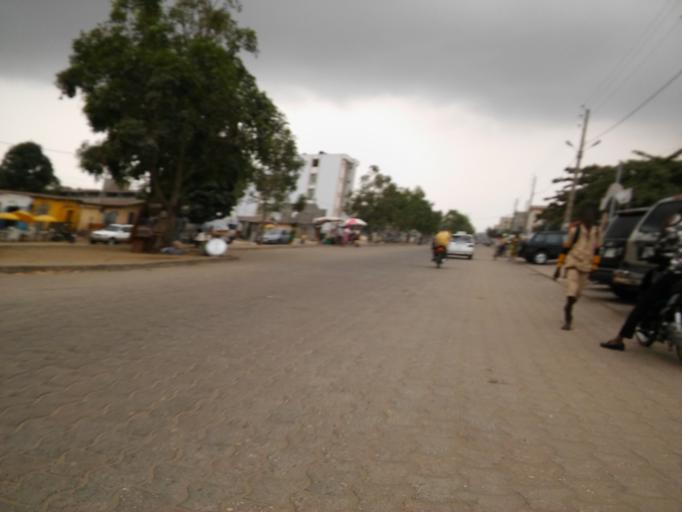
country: BJ
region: Littoral
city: Cotonou
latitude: 6.3815
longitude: 2.4017
